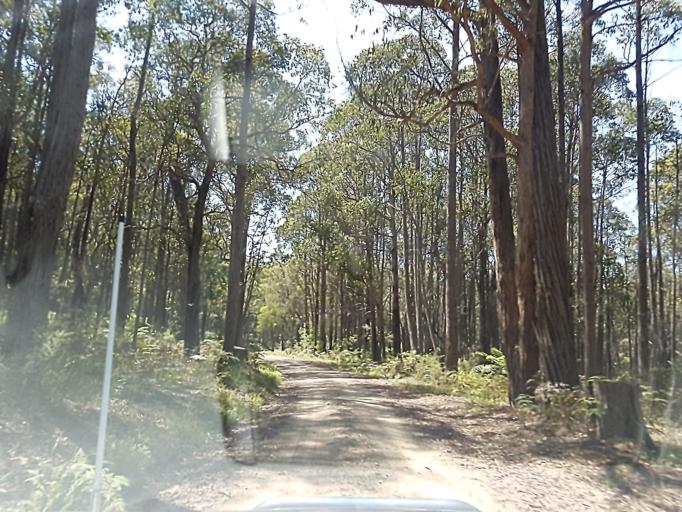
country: AU
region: Victoria
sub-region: East Gippsland
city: Lakes Entrance
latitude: -37.3000
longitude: 148.3259
